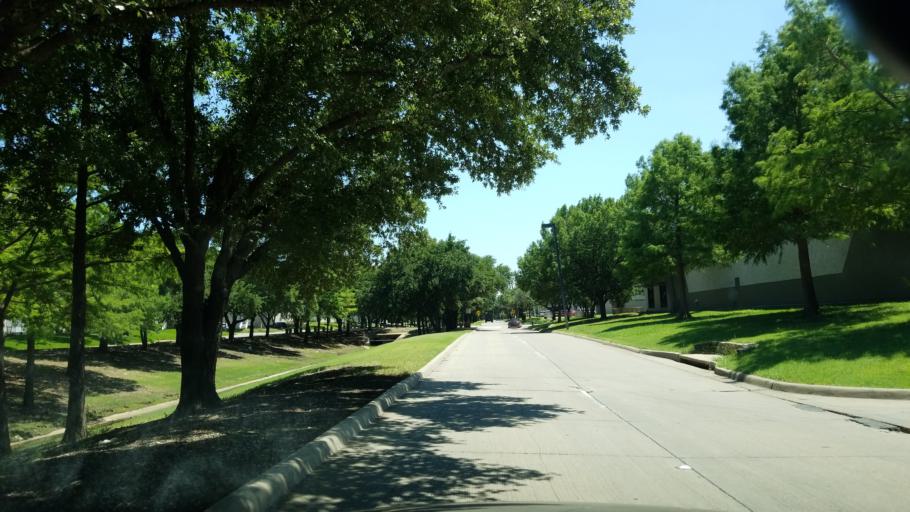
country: US
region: Texas
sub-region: Dallas County
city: Farmers Branch
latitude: 32.9333
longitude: -96.9153
